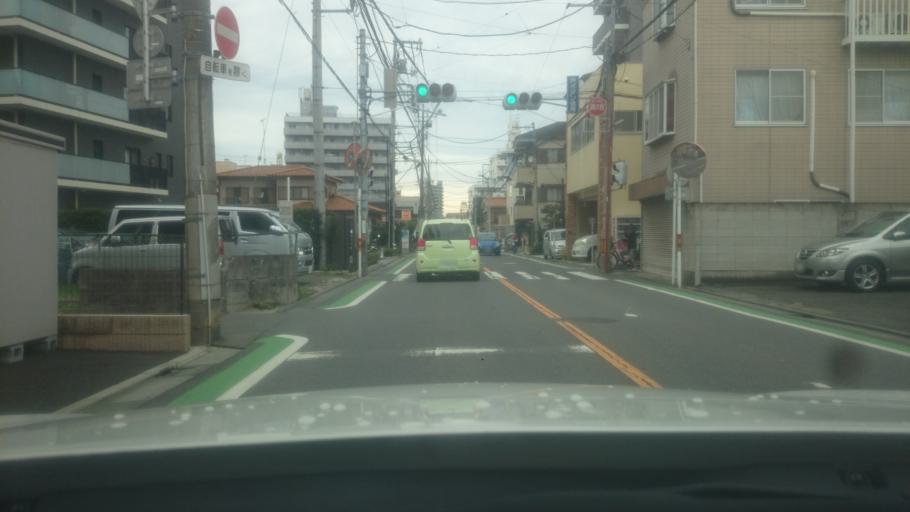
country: JP
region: Saitama
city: Kawagoe
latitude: 35.9172
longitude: 139.4854
